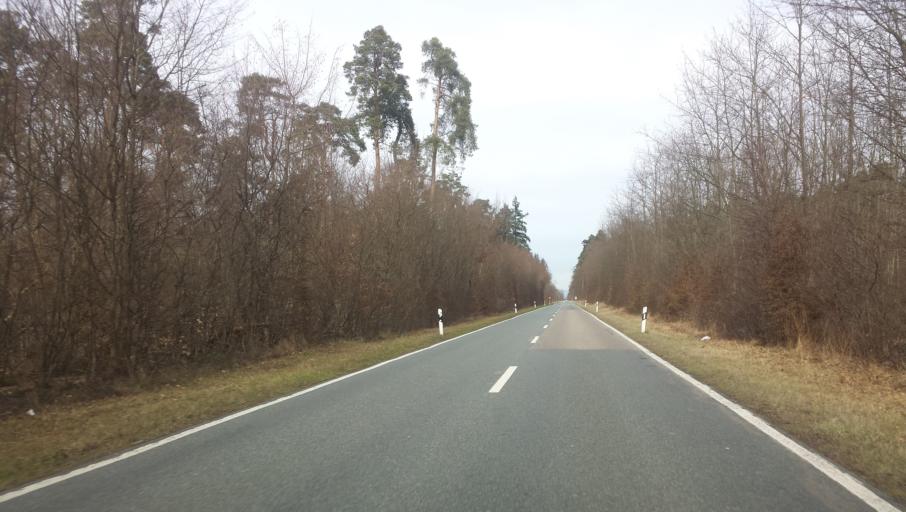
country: DE
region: Baden-Wuerttemberg
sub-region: Karlsruhe Region
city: Waghausel
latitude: 49.2583
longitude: 8.5496
